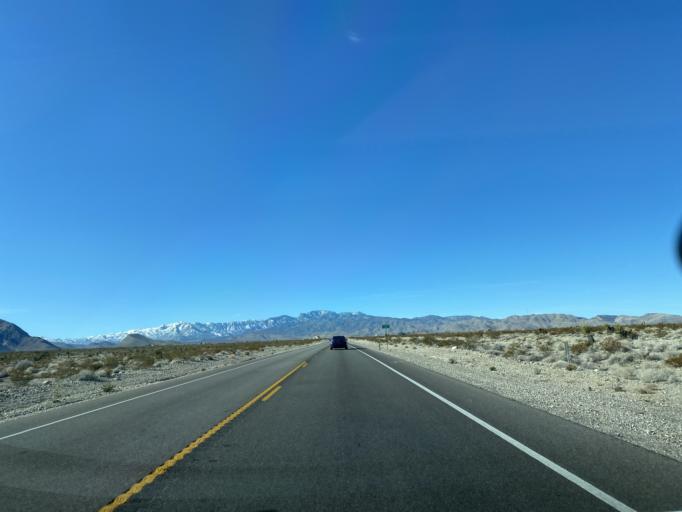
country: US
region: Nevada
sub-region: Clark County
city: Summerlin South
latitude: 36.3256
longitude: -115.3315
